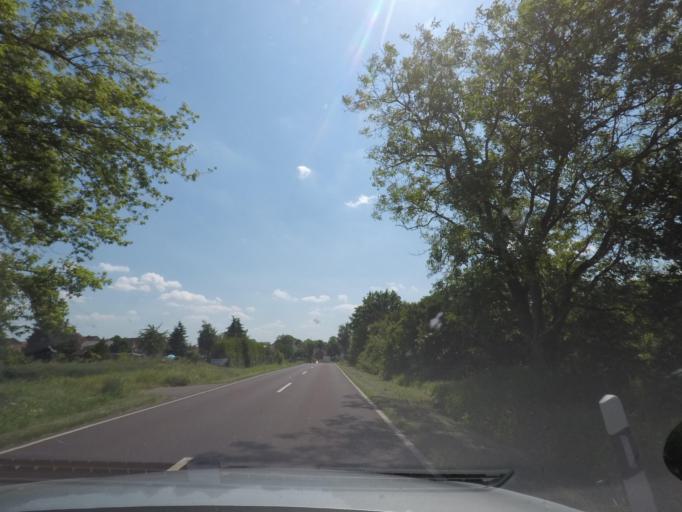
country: DE
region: Saxony-Anhalt
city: Eichenbarleben
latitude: 52.2158
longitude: 11.4010
